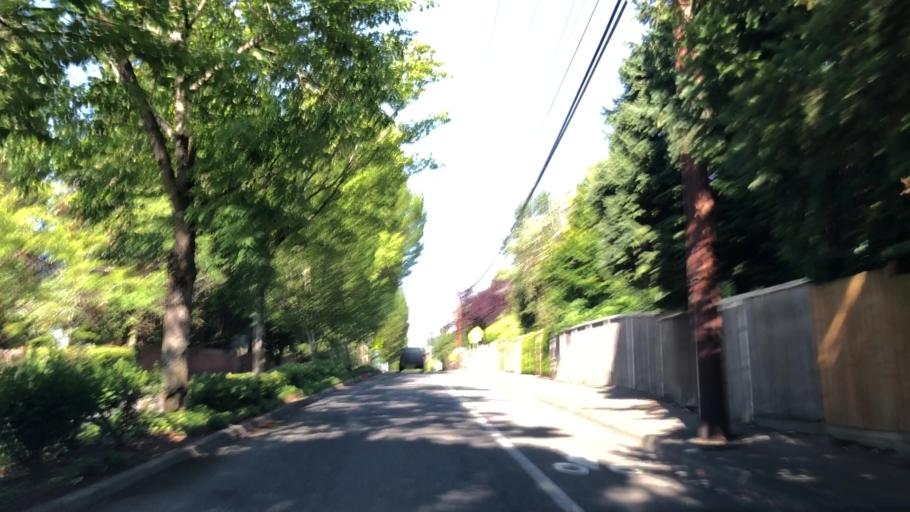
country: US
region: Washington
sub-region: King County
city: Eastgate
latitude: 47.6098
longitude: -122.1343
